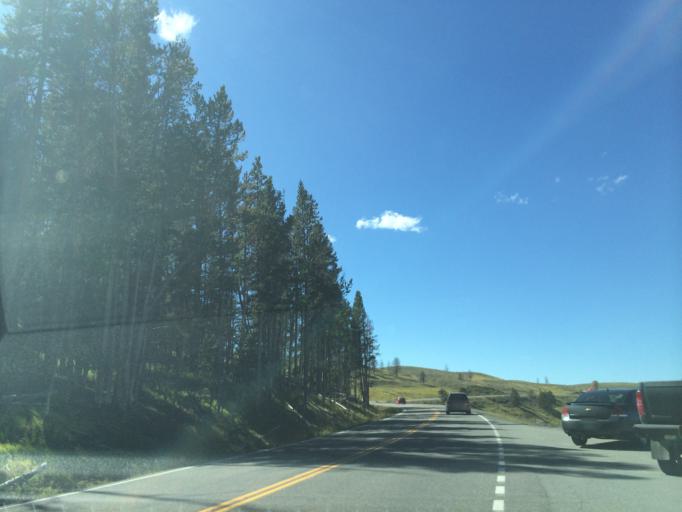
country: US
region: Montana
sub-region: Gallatin County
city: West Yellowstone
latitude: 44.6303
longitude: -110.4393
